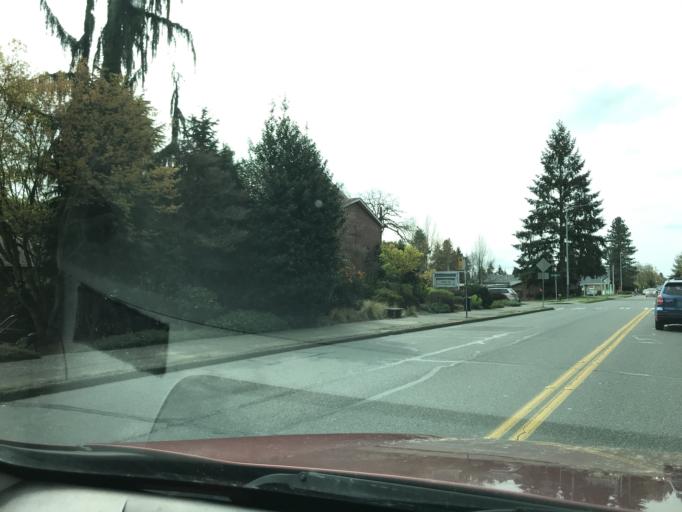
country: US
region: Washington
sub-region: King County
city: Inglewood-Finn Hill
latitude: 47.6873
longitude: -122.2907
